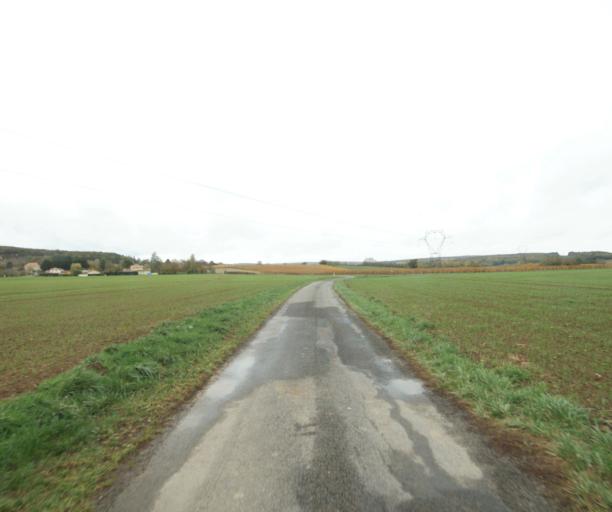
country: FR
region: Bourgogne
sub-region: Departement de Saone-et-Loire
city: Saint-Martin-Belle-Roche
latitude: 46.4688
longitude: 4.8582
